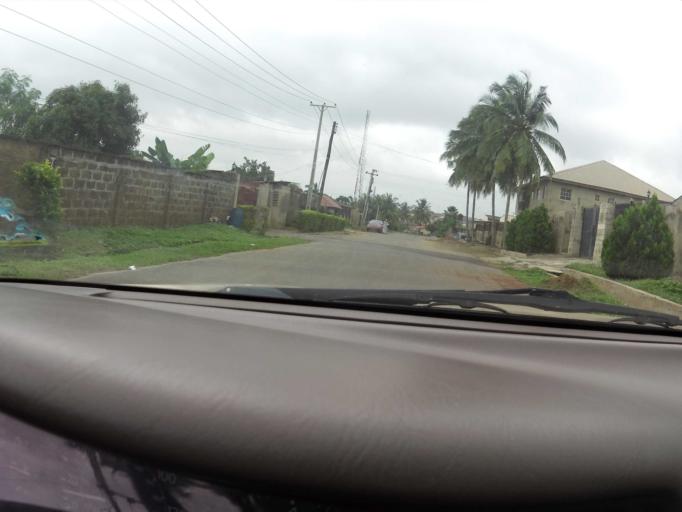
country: NG
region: Oyo
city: Ibadan
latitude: 7.4271
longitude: 3.9407
